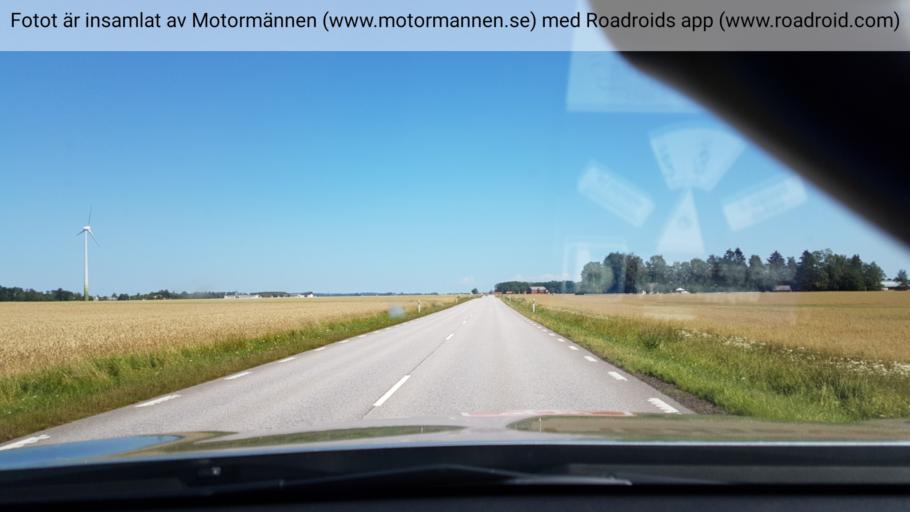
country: SE
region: Vaestra Goetaland
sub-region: Lidkopings Kommun
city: Lidkoping
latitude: 58.4259
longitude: 13.0416
